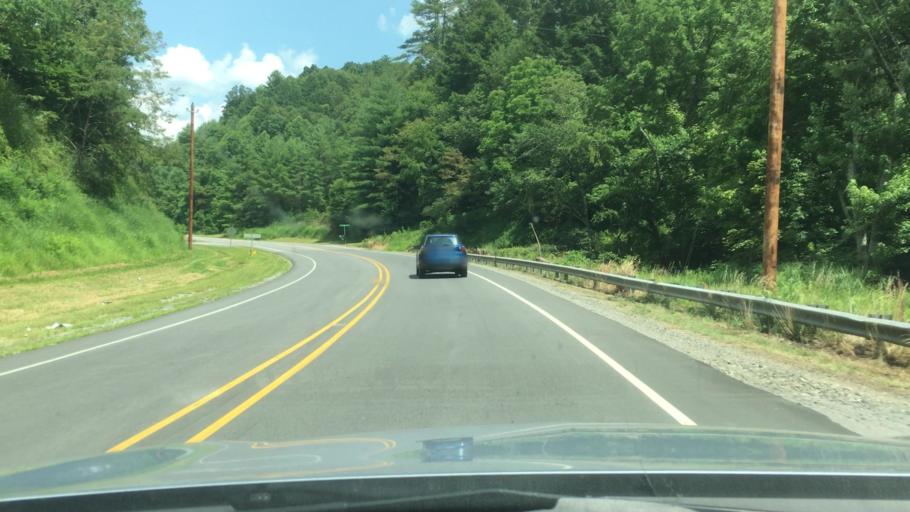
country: US
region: North Carolina
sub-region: Madison County
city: Mars Hill
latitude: 35.8219
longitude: -82.6109
